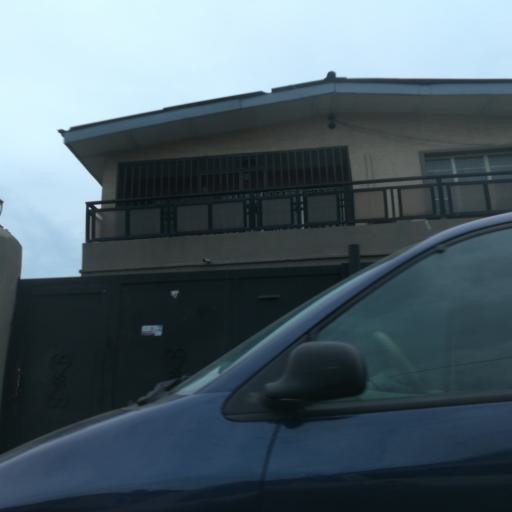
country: NG
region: Lagos
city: Makoko
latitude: 6.4998
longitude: 3.3791
